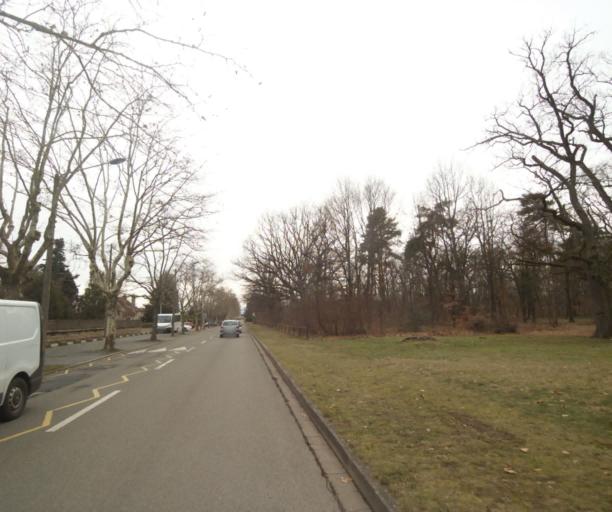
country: FR
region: Rhone-Alpes
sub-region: Departement de la Loire
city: Mably
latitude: 46.0638
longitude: 4.0778
